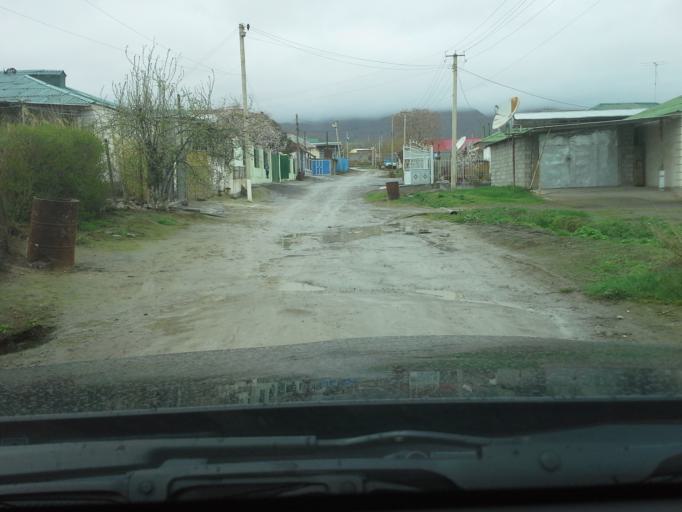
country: TM
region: Ahal
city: Abadan
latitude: 37.9623
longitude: 58.2143
